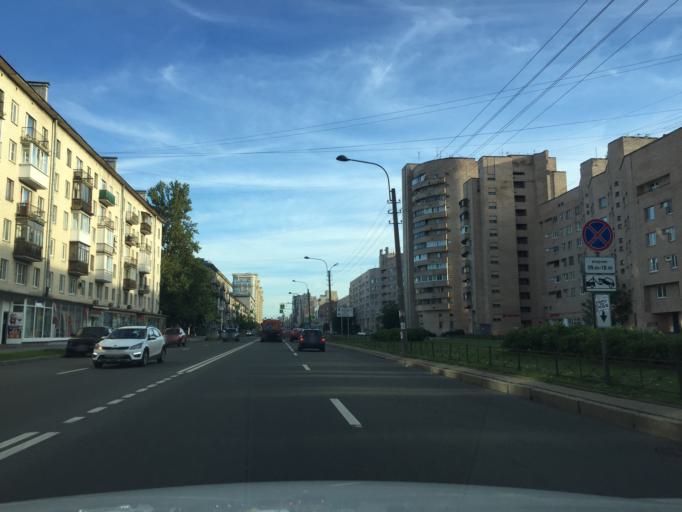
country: RU
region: St.-Petersburg
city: Kupchino
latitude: 59.8629
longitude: 30.3141
